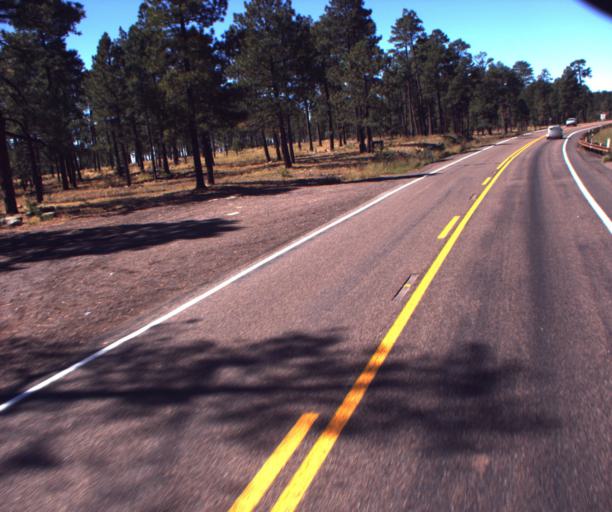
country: US
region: Arizona
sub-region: Navajo County
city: Heber-Overgaard
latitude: 34.3021
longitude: -110.8920
